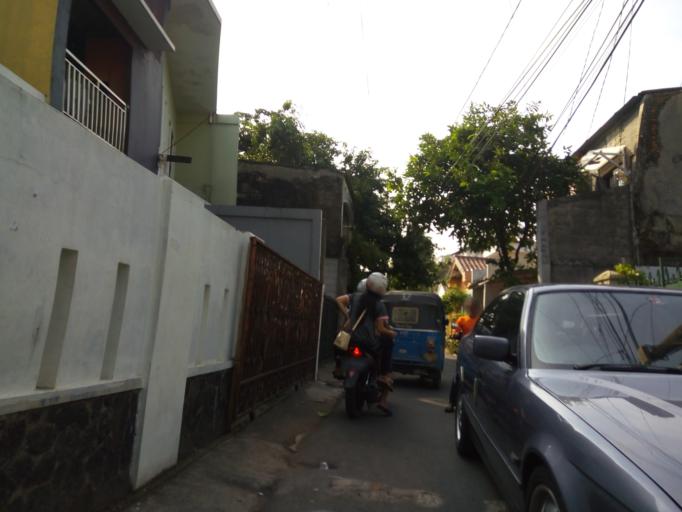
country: ID
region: Jakarta Raya
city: Jakarta
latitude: -6.2125
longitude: 106.8417
